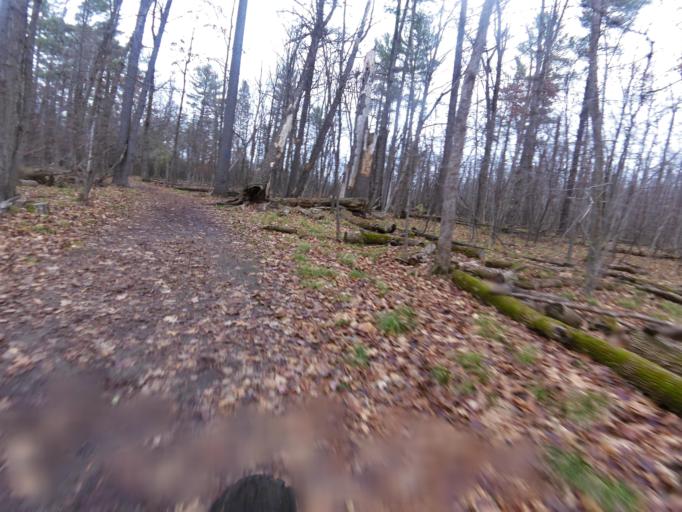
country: CA
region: Ontario
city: Bells Corners
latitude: 45.2896
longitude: -75.8098
